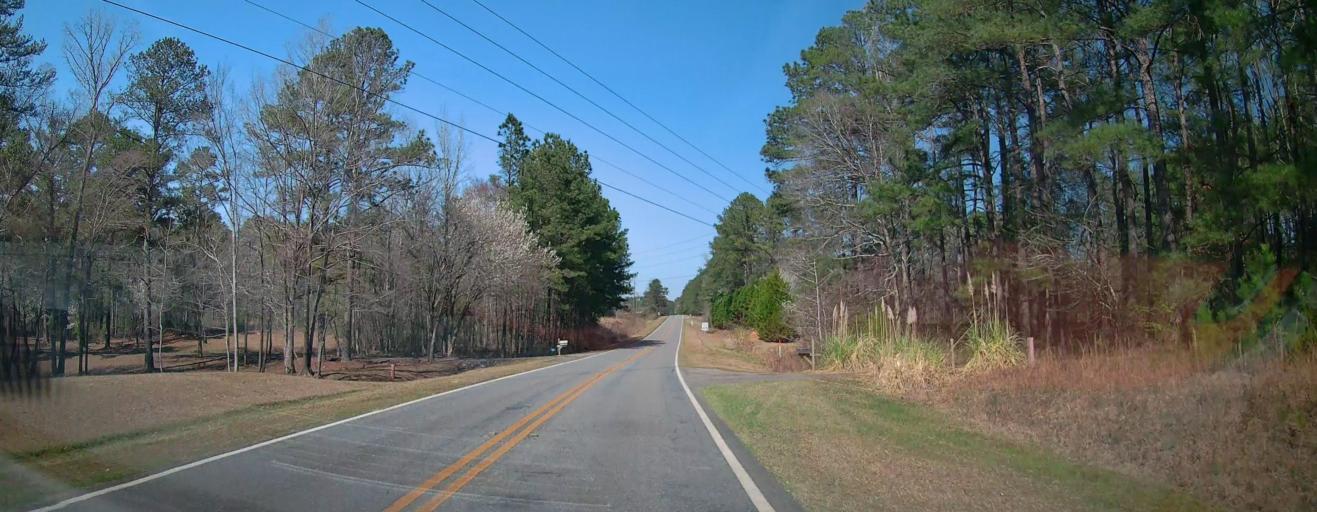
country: US
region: Georgia
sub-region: Jones County
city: Gray
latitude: 32.9722
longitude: -83.5479
